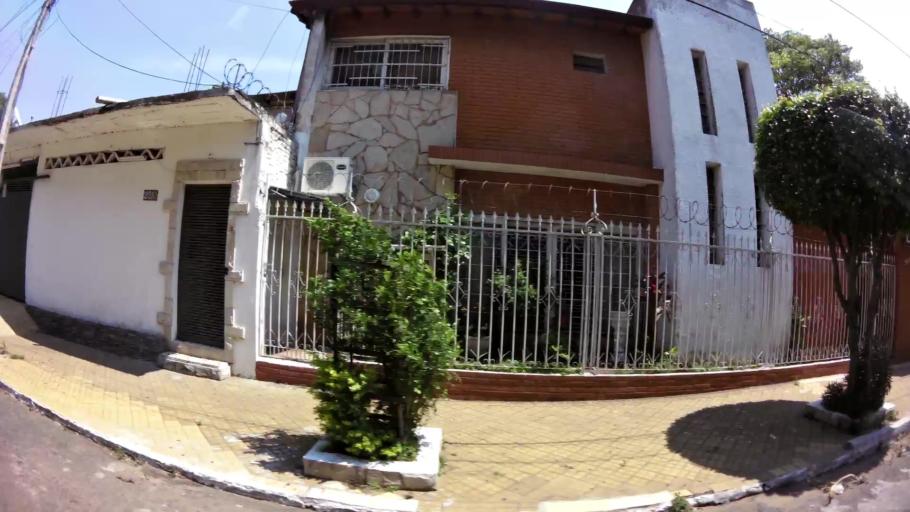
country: PY
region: Asuncion
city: Asuncion
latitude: -25.2996
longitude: -57.6462
